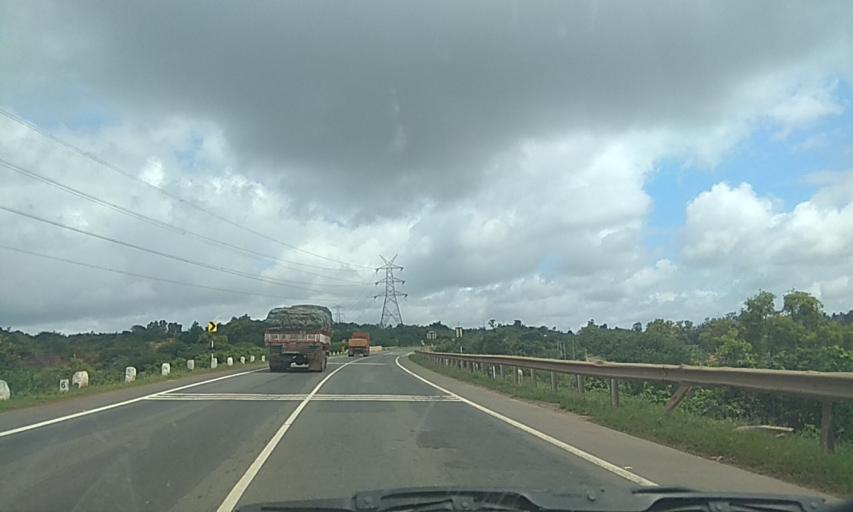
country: IN
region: Karnataka
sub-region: Dharwad
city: Hubli
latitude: 15.4303
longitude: 74.9673
